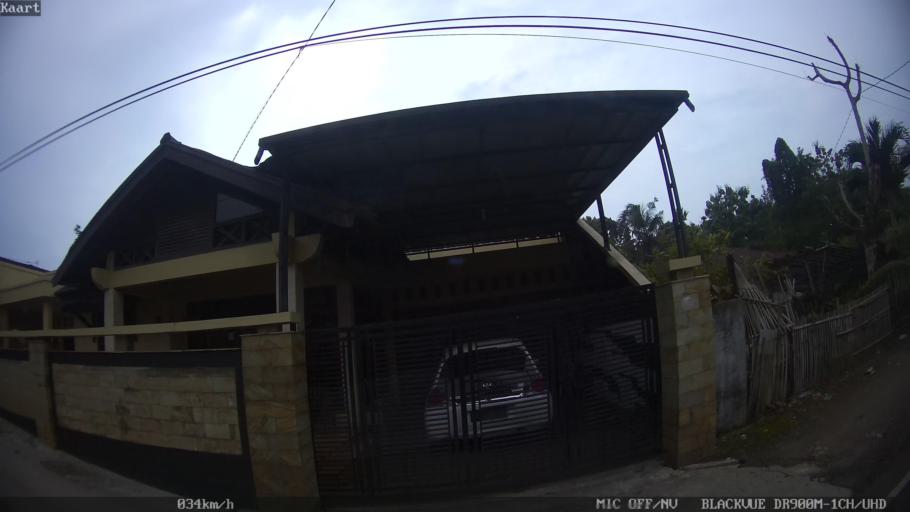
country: ID
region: Lampung
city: Kedaton
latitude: -5.3903
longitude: 105.2326
